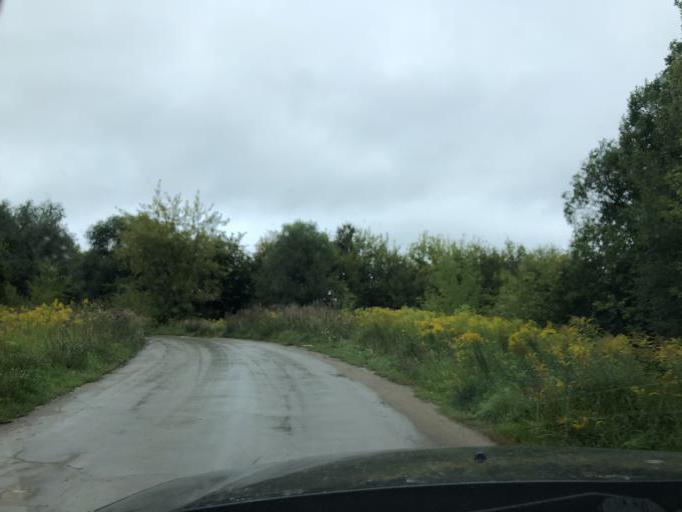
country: RU
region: Tula
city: Mendeleyevskiy
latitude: 54.1719
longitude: 37.5530
